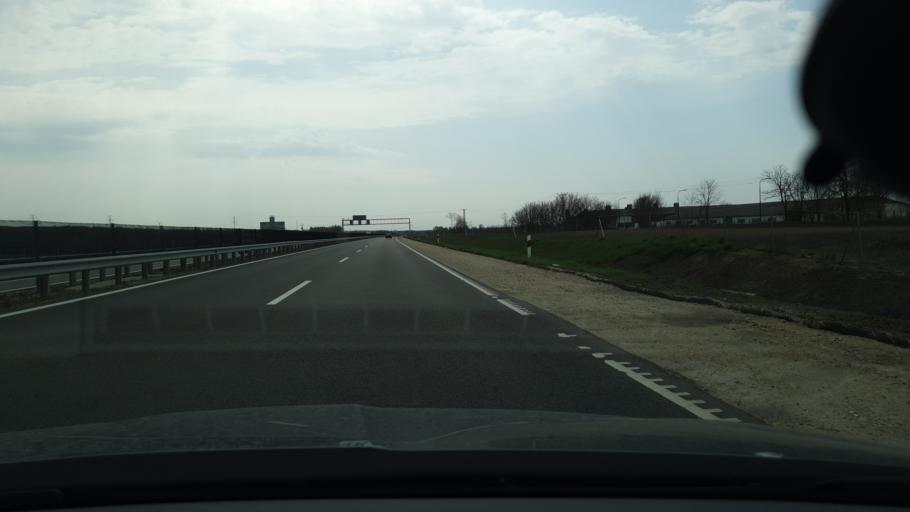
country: HU
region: Pest
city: Pilis
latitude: 47.3023
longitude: 19.5662
